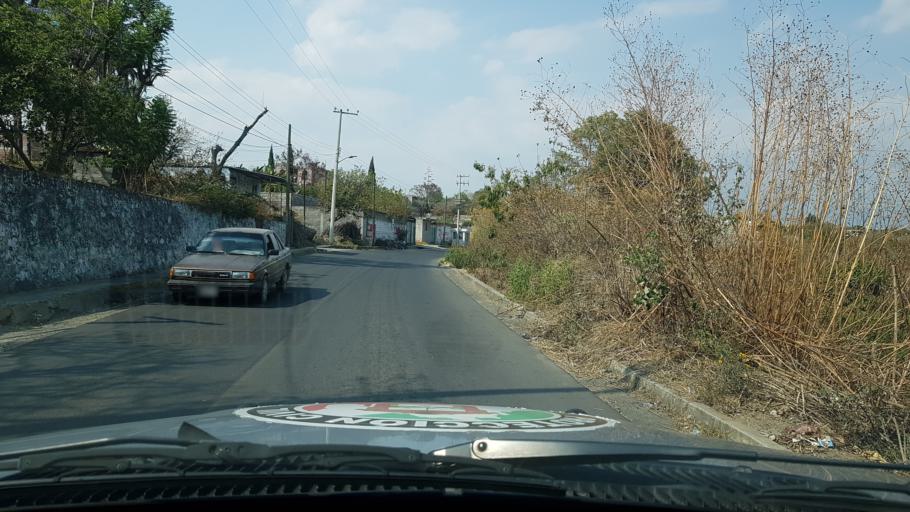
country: MX
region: Mexico
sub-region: Atlautla
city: San Andres Tlalamac
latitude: 18.9763
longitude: -98.8134
